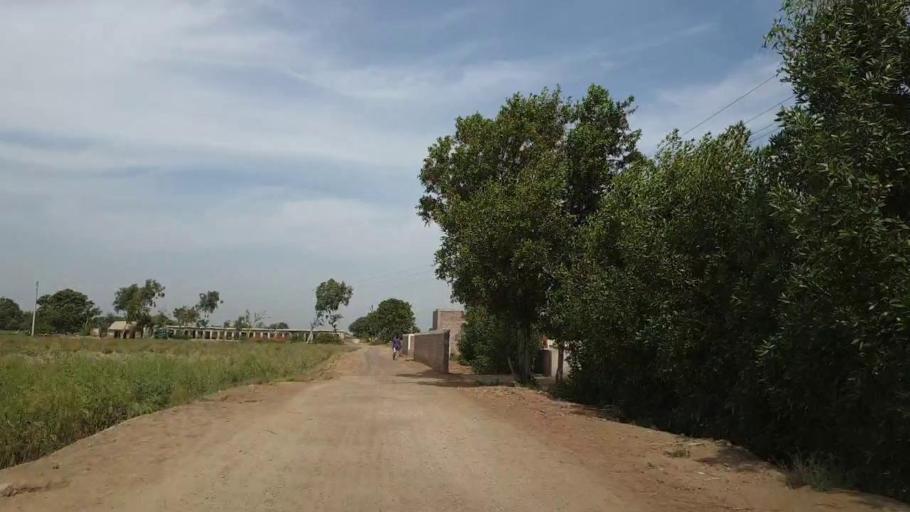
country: PK
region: Sindh
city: Kunri
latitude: 25.2162
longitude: 69.5839
